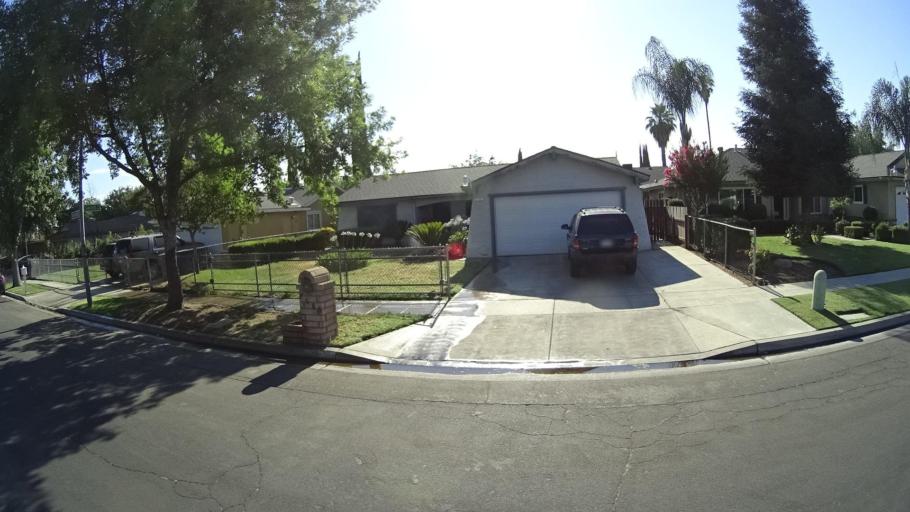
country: US
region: California
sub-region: Fresno County
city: Fresno
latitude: 36.7083
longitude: -119.7416
